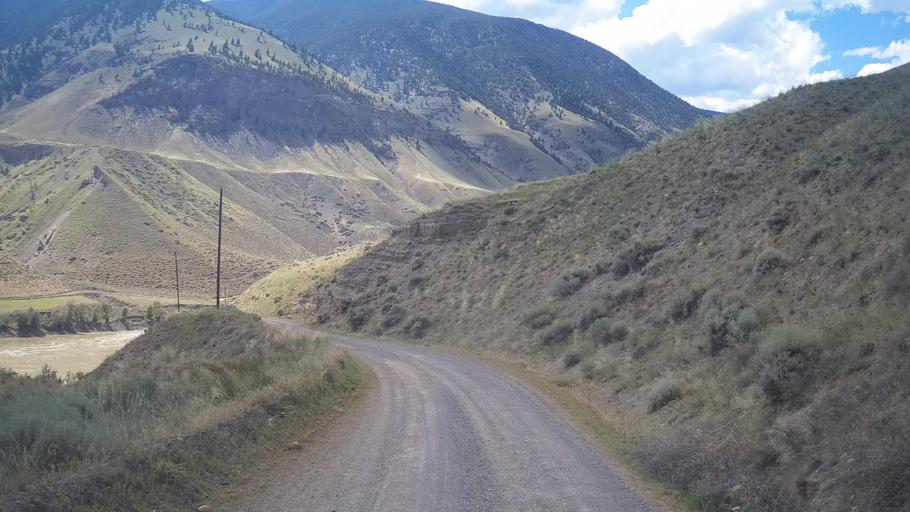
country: CA
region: British Columbia
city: Lillooet
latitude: 51.1816
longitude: -122.1217
